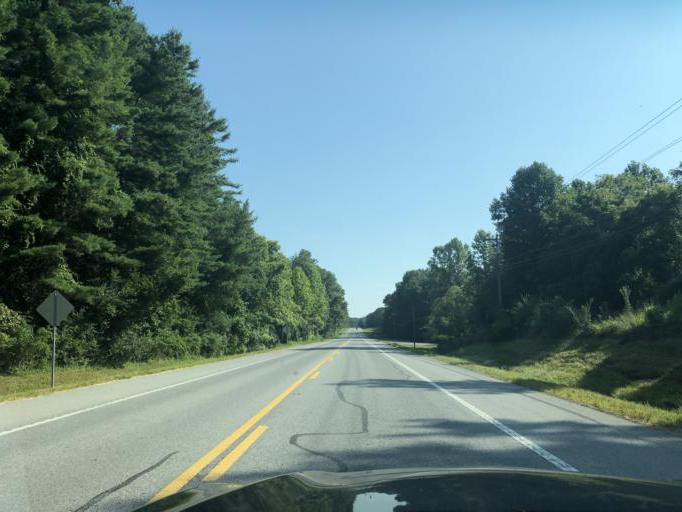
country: US
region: Tennessee
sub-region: Franklin County
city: Sewanee
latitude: 35.1985
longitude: -85.9103
